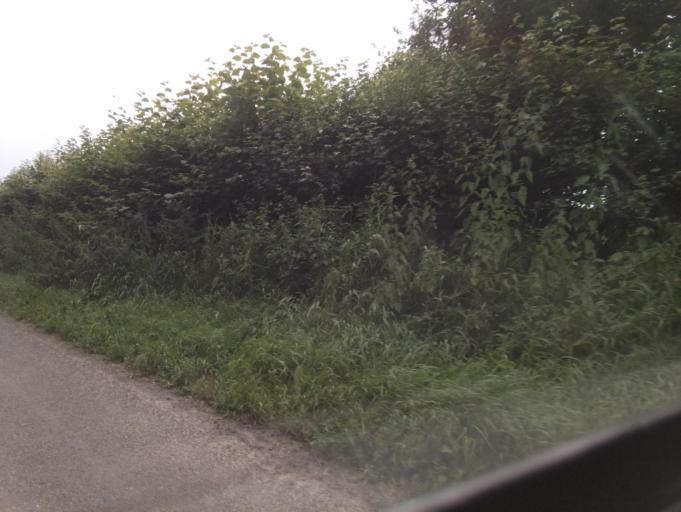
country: GB
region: England
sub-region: Devon
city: Colyton
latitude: 50.7242
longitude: -3.0478
